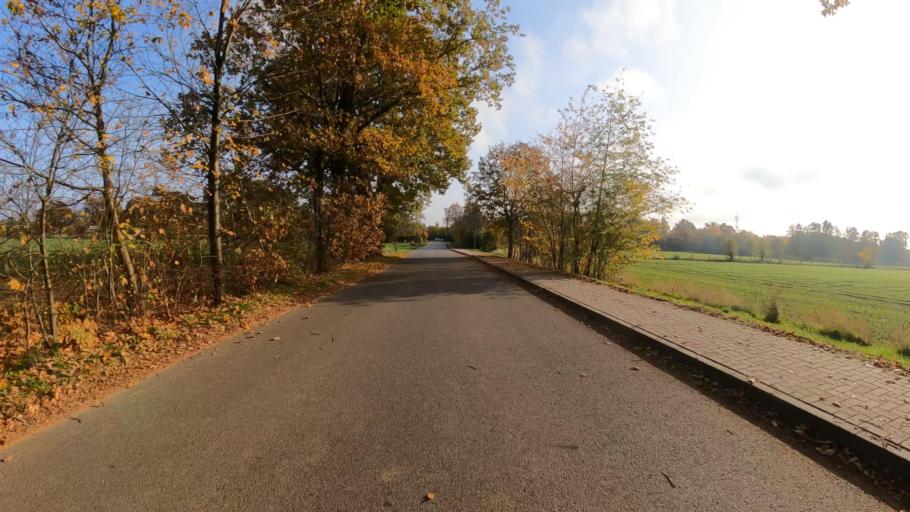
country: DE
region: Lower Saxony
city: Buchholz in der Nordheide
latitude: 53.3323
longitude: 9.8405
